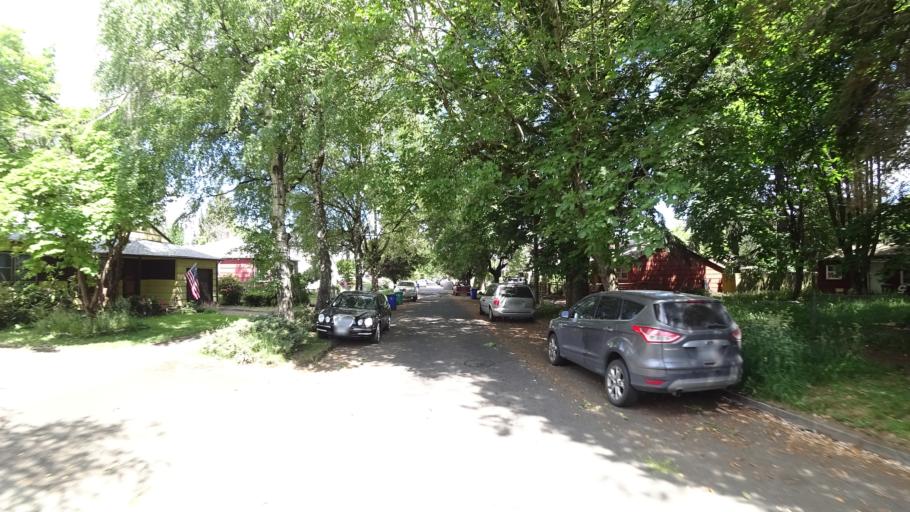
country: US
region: Oregon
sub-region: Washington County
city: West Haven
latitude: 45.5973
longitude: -122.7596
